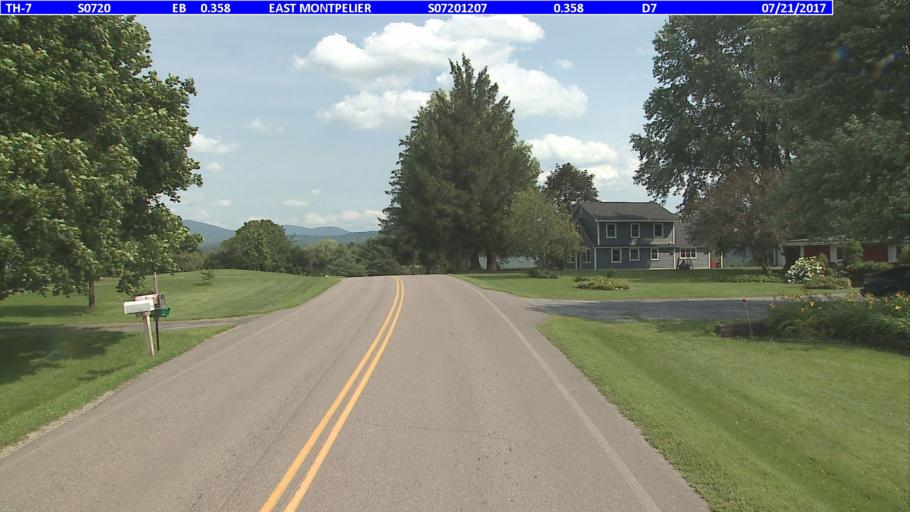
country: US
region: Vermont
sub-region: Washington County
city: Barre
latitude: 44.2747
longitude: -72.4938
